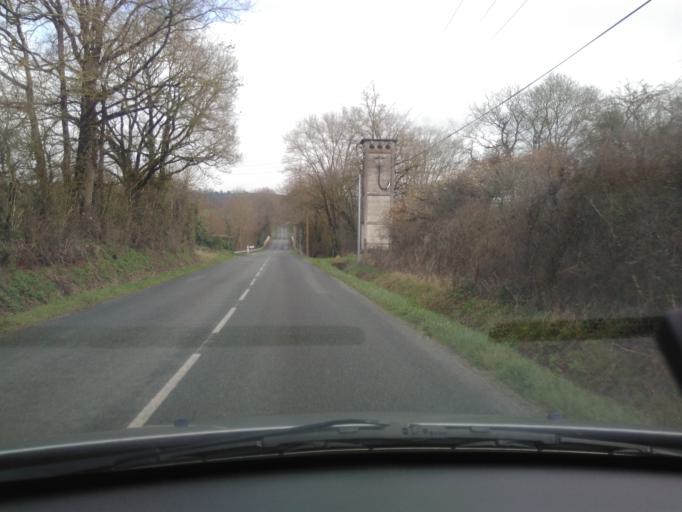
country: FR
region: Pays de la Loire
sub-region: Departement de la Vendee
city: Sainte-Cecile
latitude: 46.6997
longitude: -1.1263
